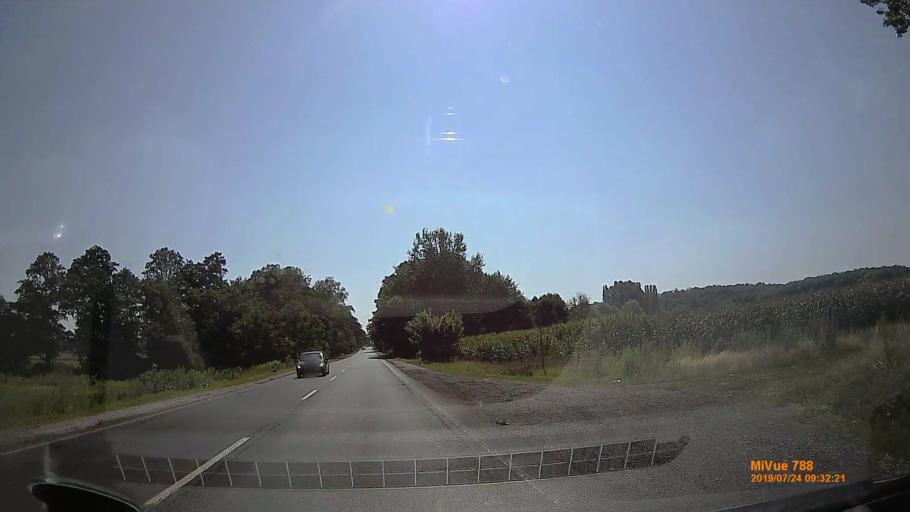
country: HU
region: Szabolcs-Szatmar-Bereg
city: Napkor
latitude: 47.9509
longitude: 21.8285
